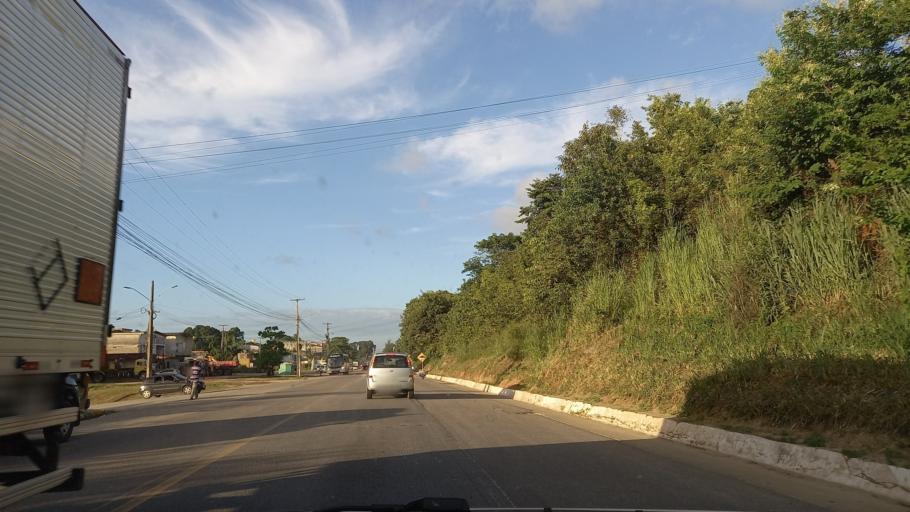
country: BR
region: Pernambuco
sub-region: Cabo De Santo Agostinho
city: Cabo
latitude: -8.2424
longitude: -34.9887
